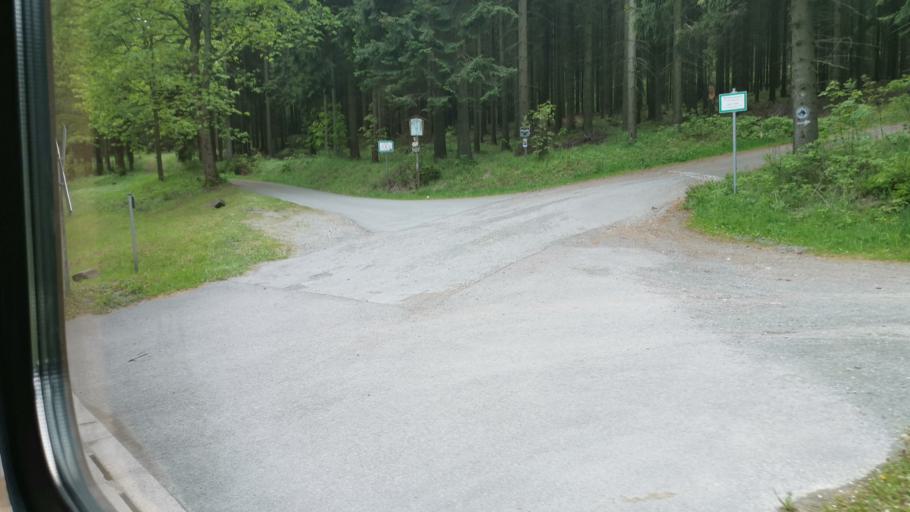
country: CZ
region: Ustecky
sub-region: Okres Chomutov
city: Vejprty
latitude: 50.4645
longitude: 13.0139
